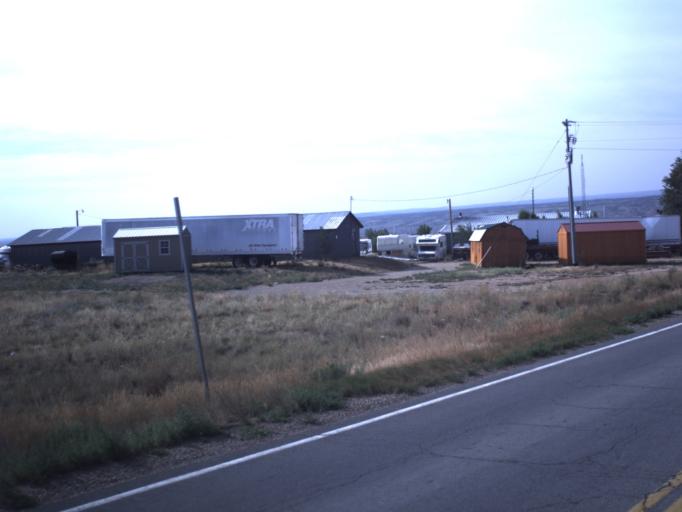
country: US
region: Utah
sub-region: Duchesne County
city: Duchesne
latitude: 40.1918
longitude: -110.3933
